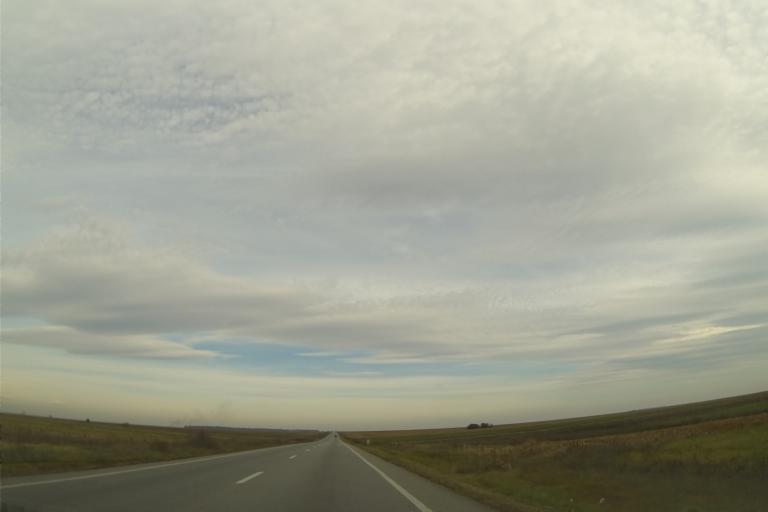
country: RO
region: Olt
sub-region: Comuna Priseaca
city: Priseaca
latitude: 44.4925
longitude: 24.4482
